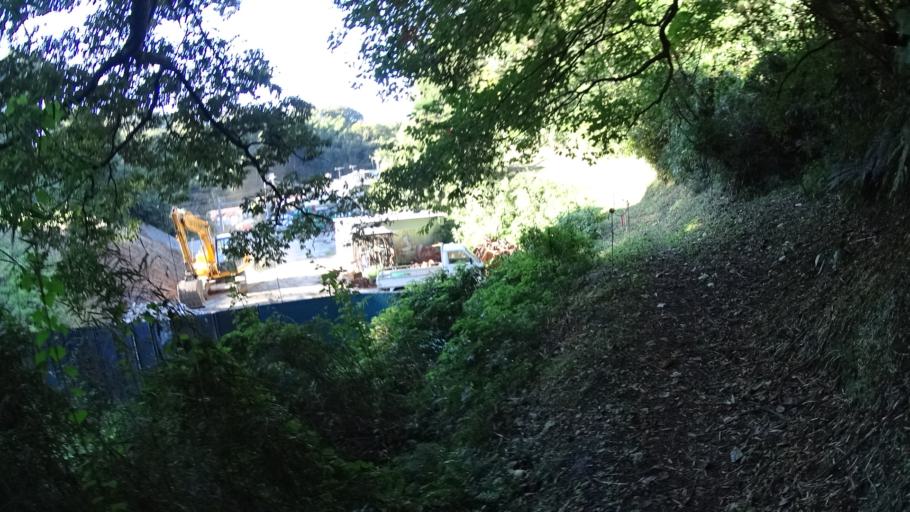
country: JP
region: Kanagawa
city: Kamakura
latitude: 35.3656
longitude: 139.6012
